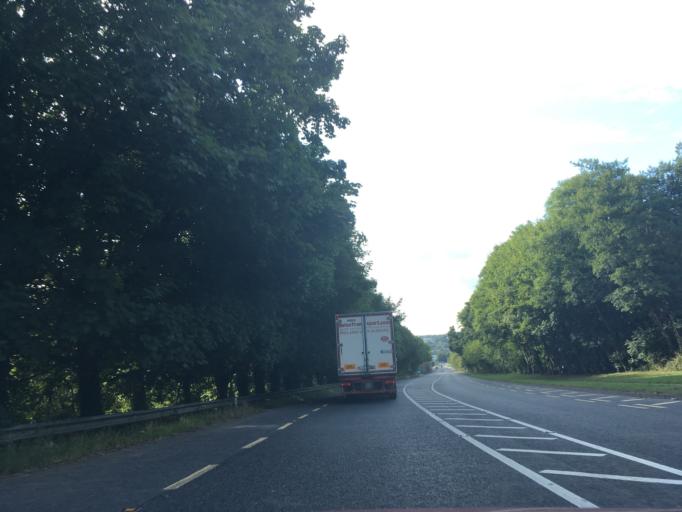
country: IE
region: Leinster
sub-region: Loch Garman
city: New Ross
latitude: 52.3825
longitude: -6.9441
